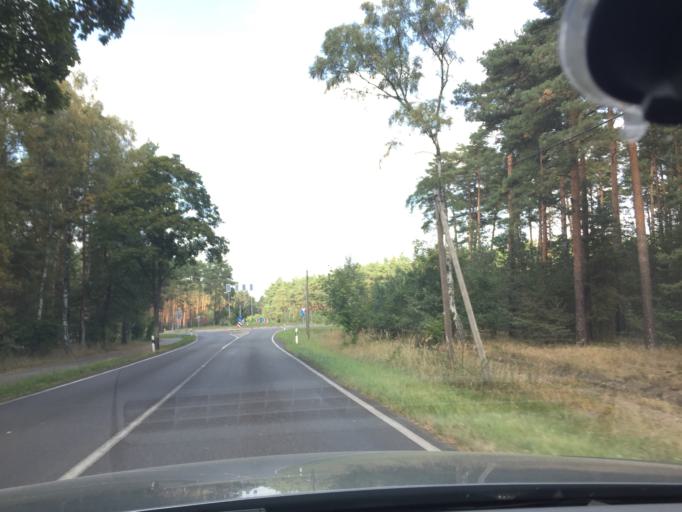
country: DE
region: Brandenburg
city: Grunheide
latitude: 52.3907
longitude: 13.8263
